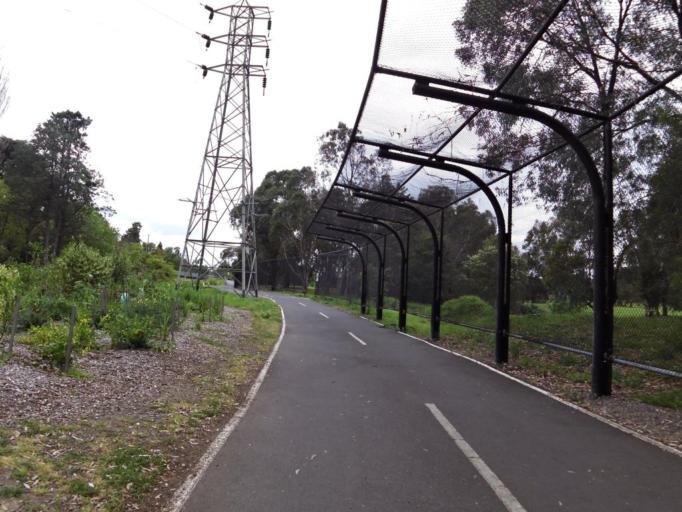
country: AU
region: Victoria
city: Carnegie
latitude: -37.8745
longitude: 145.0690
